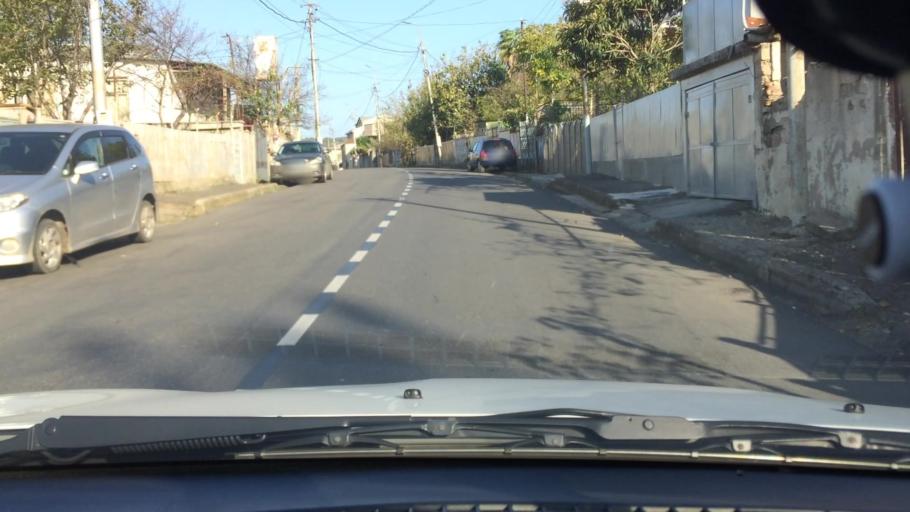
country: GE
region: Imereti
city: Kutaisi
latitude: 42.2704
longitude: 42.7138
